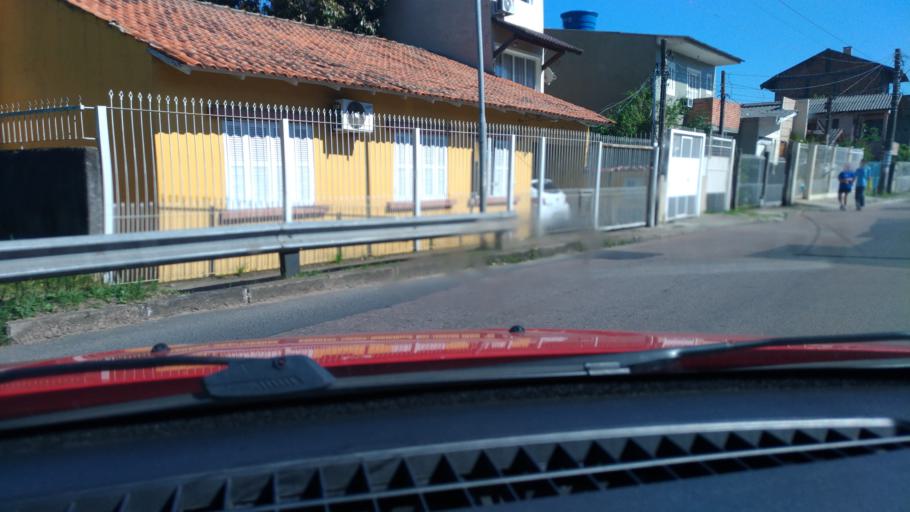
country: BR
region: Rio Grande do Sul
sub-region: Cachoeirinha
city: Cachoeirinha
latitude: -30.0366
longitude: -51.1274
